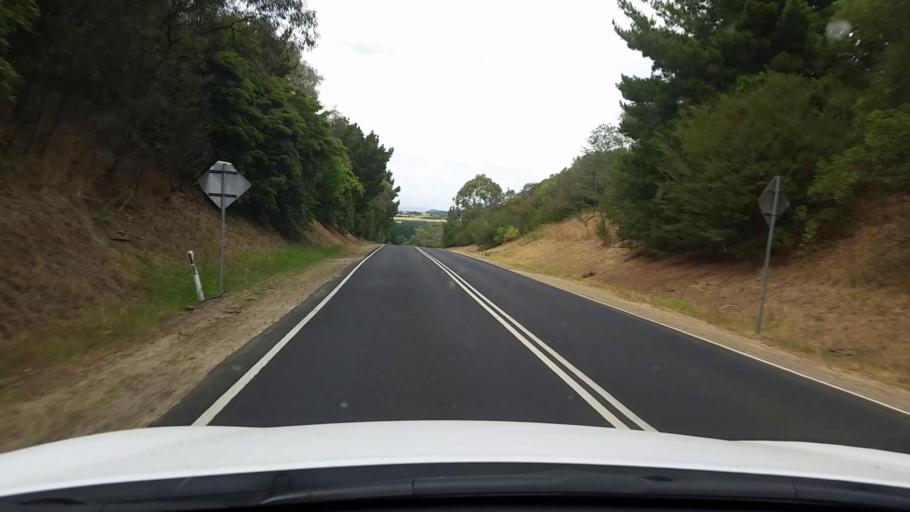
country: AU
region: Victoria
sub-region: Mornington Peninsula
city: Merricks
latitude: -38.4220
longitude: 145.0437
